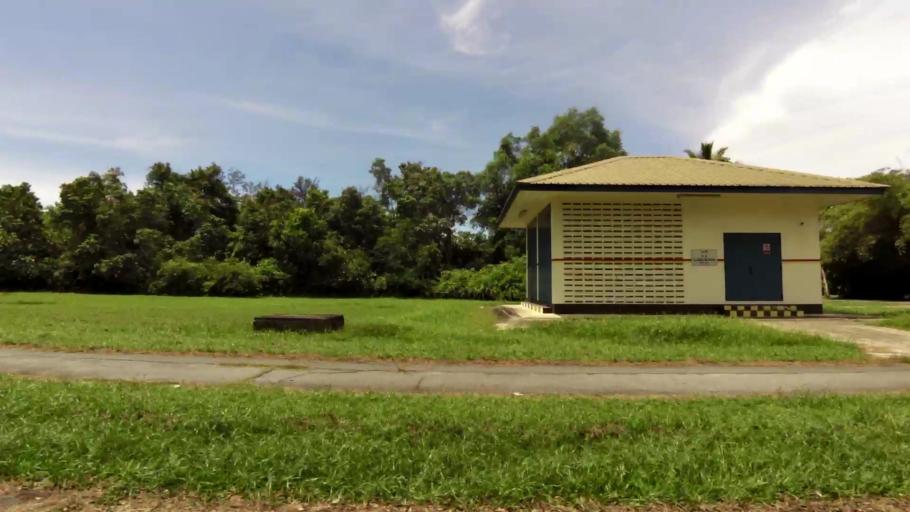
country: BN
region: Belait
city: Kuala Belait
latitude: 4.5993
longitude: 114.2754
